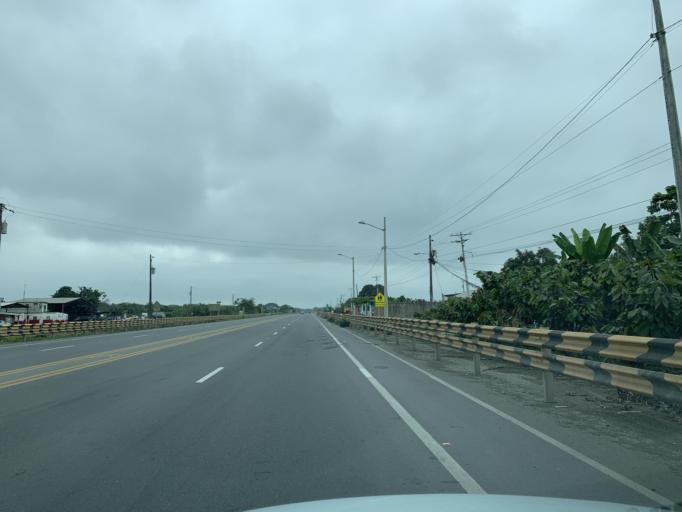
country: EC
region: Guayas
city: Coronel Marcelino Mariduena
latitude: -2.2934
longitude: -79.5014
